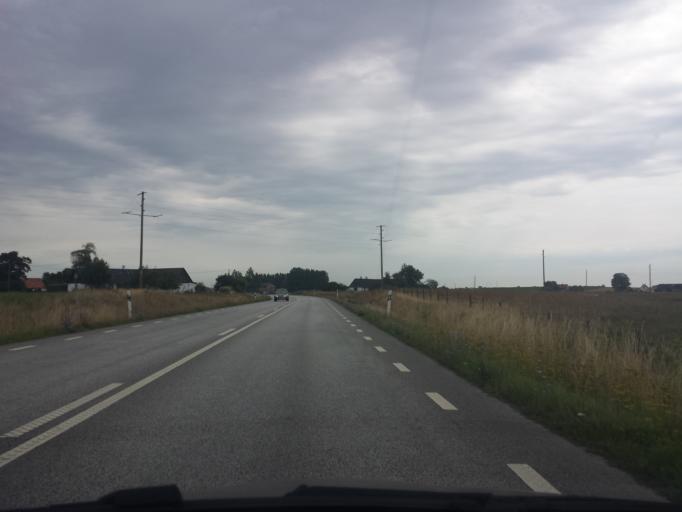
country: SE
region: Skane
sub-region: Ystads Kommun
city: Kopingebro
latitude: 55.4343
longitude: 13.9769
